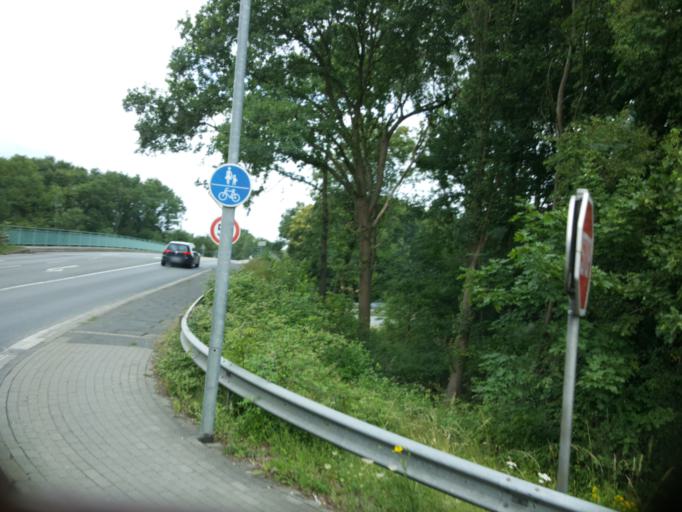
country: DE
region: North Rhine-Westphalia
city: Bad Oeynhausen
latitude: 52.2034
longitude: 8.7597
